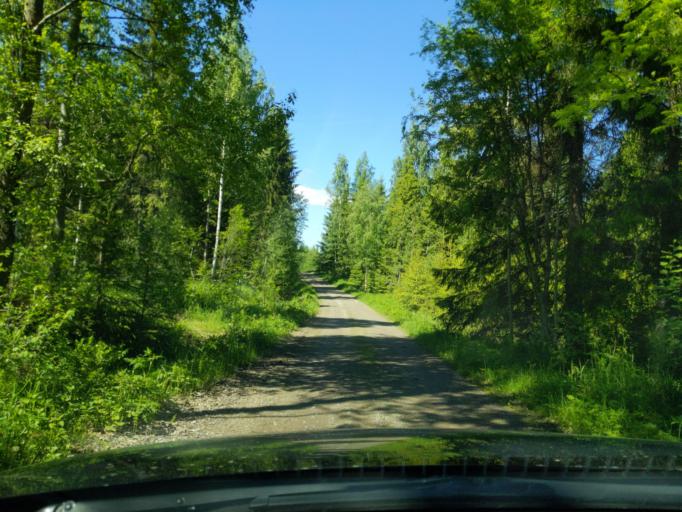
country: FI
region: Paijanne Tavastia
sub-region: Lahti
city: Lahti
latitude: 61.0541
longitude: 25.6927
